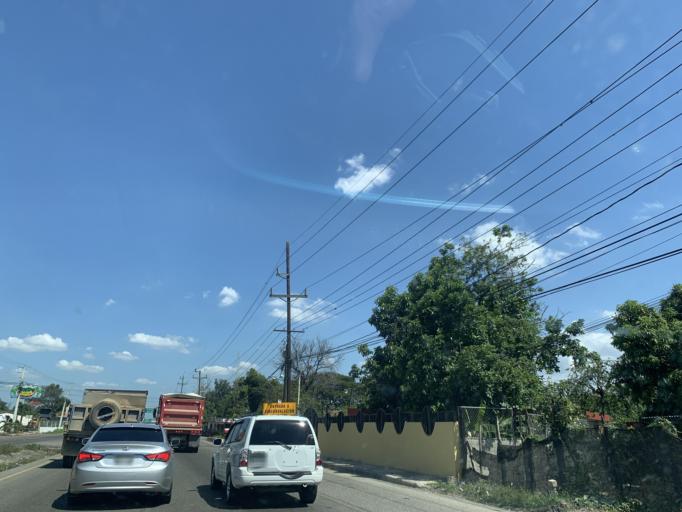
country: DO
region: Santiago
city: Villa Gonzalez
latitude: 19.5208
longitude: -70.7666
